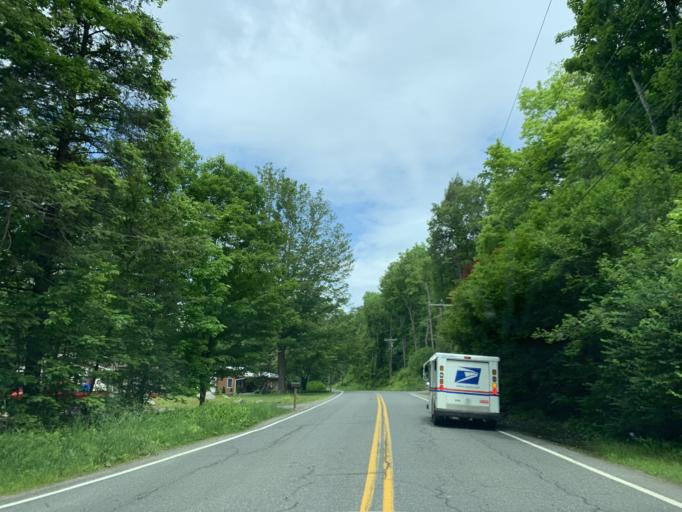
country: US
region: Massachusetts
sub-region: Hampshire County
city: Westhampton
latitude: 42.2391
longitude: -72.8556
